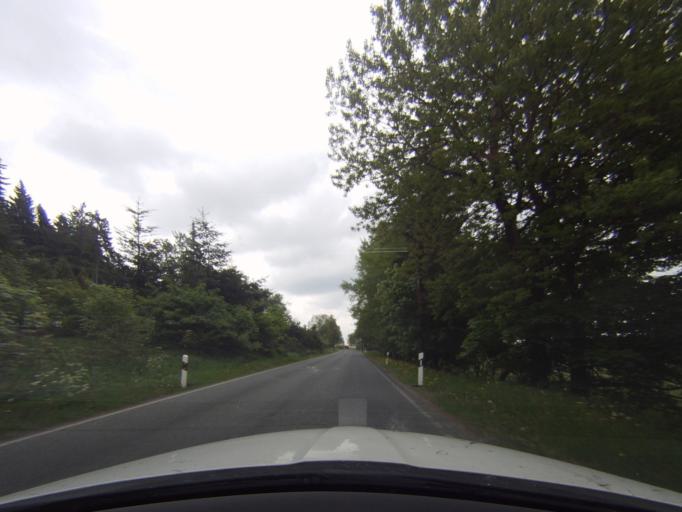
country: DE
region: Thuringia
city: Gillersdorf
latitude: 50.6175
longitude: 11.0279
